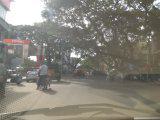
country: IN
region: Karnataka
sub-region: Bangalore Urban
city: Bangalore
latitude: 12.9864
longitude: 77.5408
